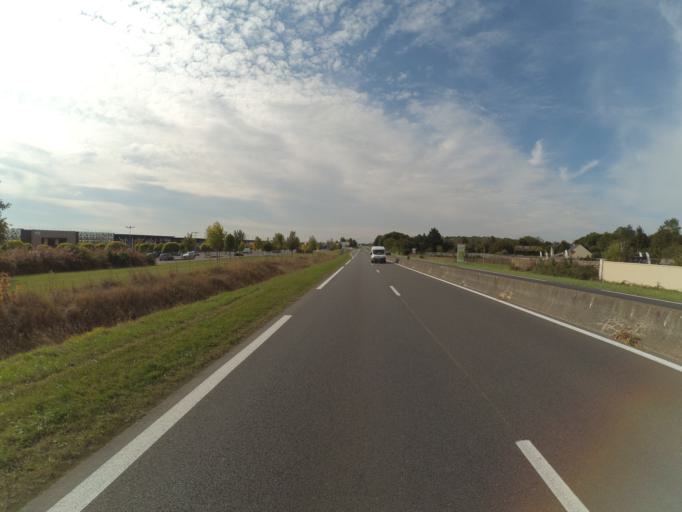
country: FR
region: Pays de la Loire
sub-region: Departement de Maine-et-Loire
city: Distre
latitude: 47.2342
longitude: -0.1148
